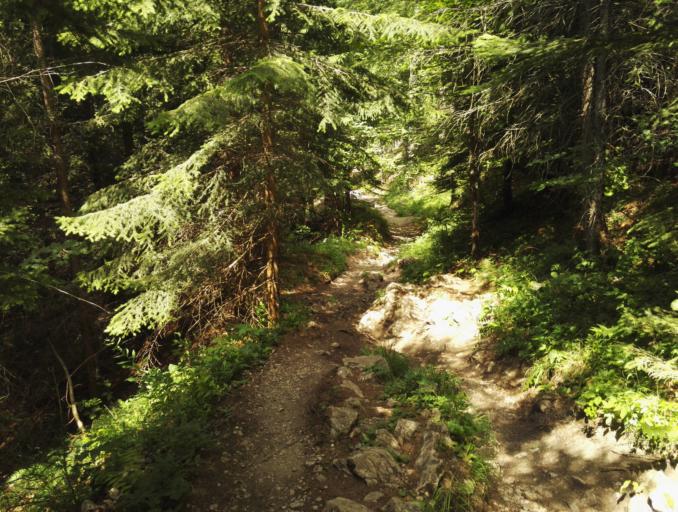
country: AT
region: Styria
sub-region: Politischer Bezirk Graz-Umgebung
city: Rothelstein
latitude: 47.3463
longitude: 15.3985
